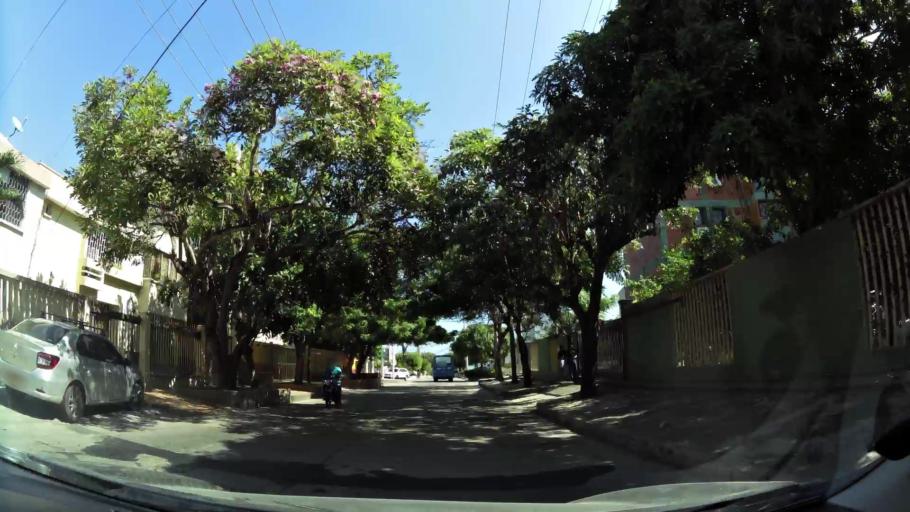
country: CO
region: Atlantico
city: Barranquilla
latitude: 11.0176
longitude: -74.8121
